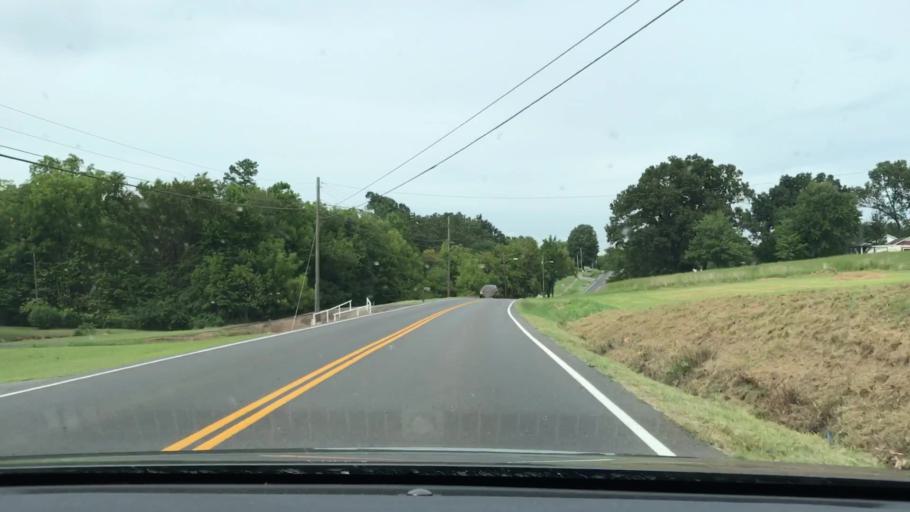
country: US
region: Kentucky
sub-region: Marshall County
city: Benton
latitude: 36.8380
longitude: -88.3507
